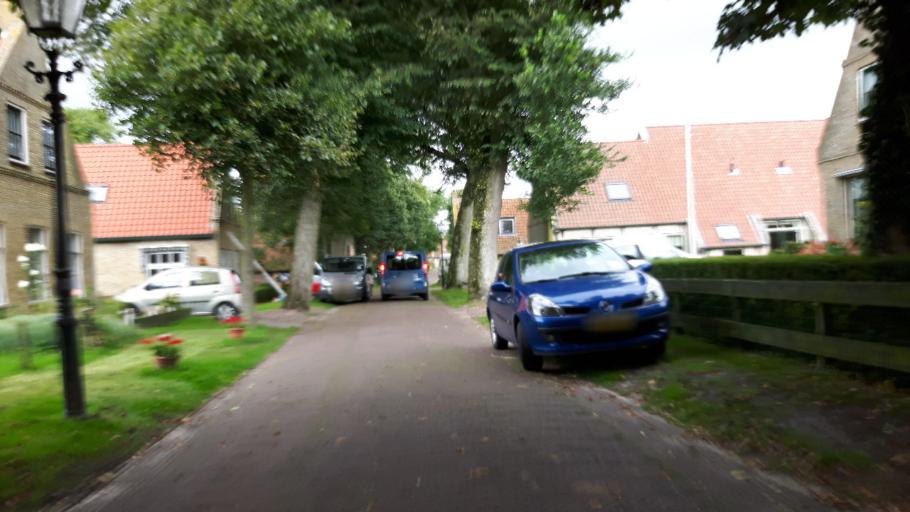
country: NL
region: Friesland
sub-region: Gemeente Ameland
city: Hollum
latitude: 53.4367
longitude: 5.6414
